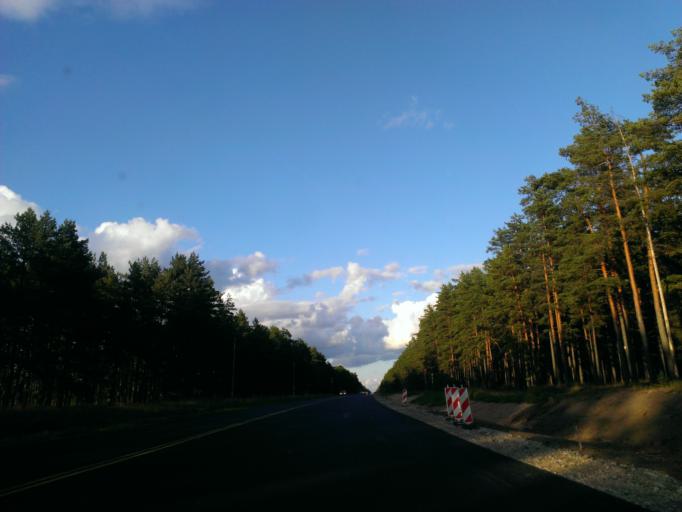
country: LV
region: Garkalne
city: Garkalne
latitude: 57.0592
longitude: 24.4600
